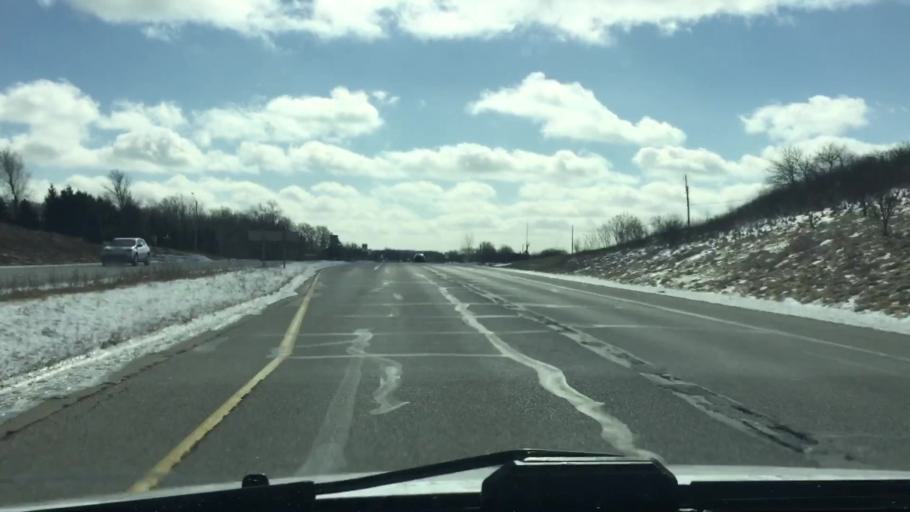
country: US
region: Wisconsin
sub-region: Waukesha County
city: Big Bend
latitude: 42.9349
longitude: -88.2286
